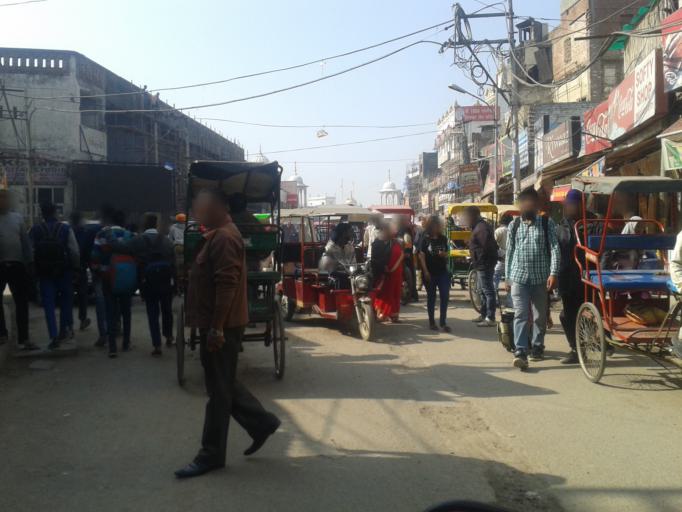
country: IN
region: Punjab
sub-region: Amritsar
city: Amritsar
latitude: 31.6215
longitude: 74.8792
